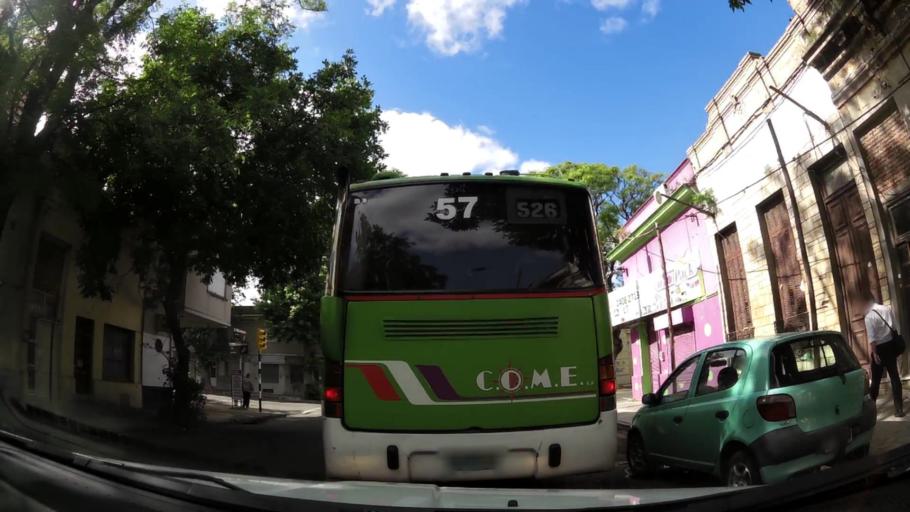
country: UY
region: Montevideo
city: Montevideo
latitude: -34.8925
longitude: -56.1788
